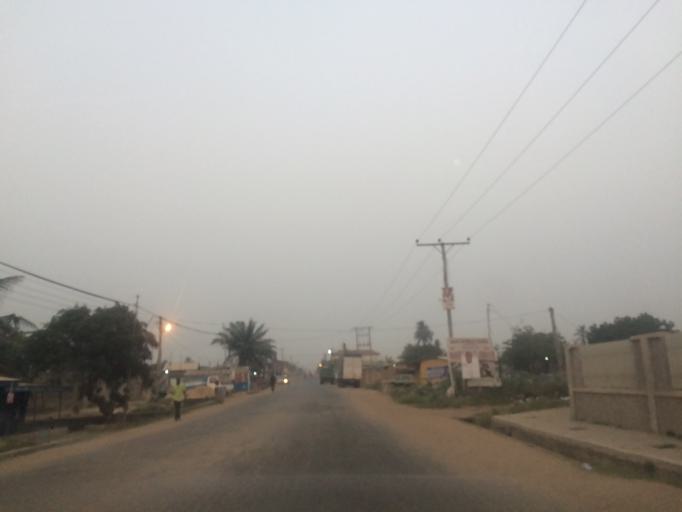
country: GH
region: Greater Accra
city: Teshi Old Town
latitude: 5.5914
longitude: -0.1020
